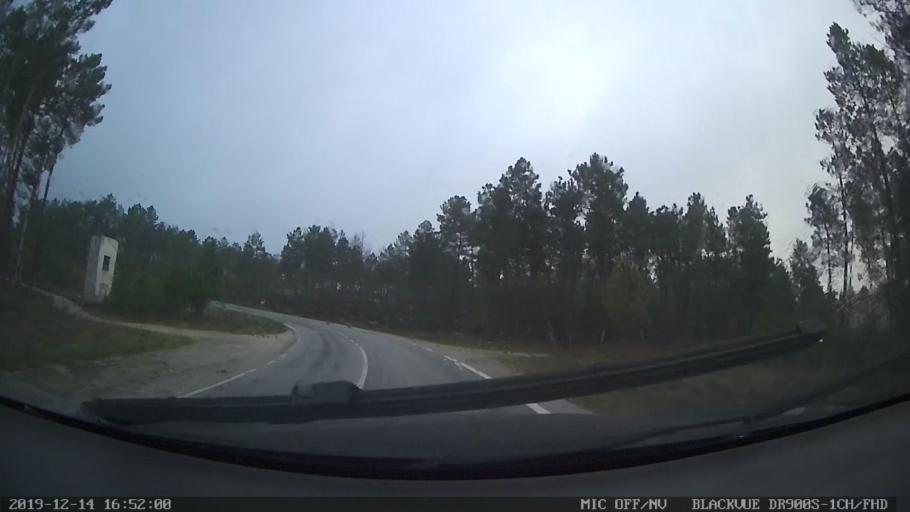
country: PT
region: Vila Real
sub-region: Murca
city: Murca
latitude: 41.4269
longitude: -7.5049
